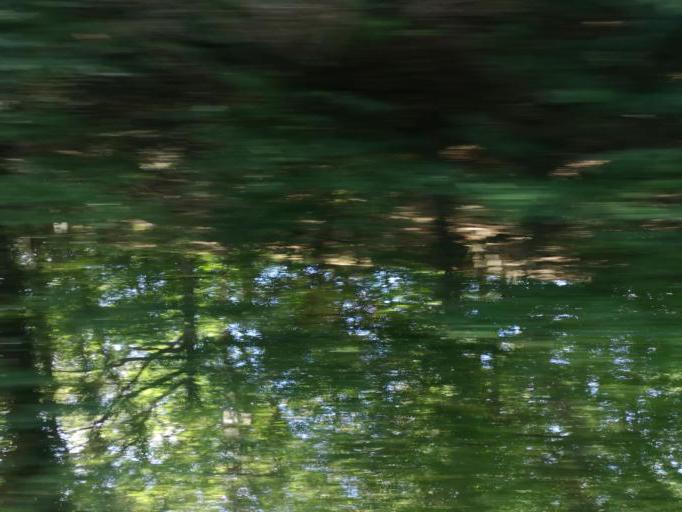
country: DE
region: North Rhine-Westphalia
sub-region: Regierungsbezirk Koln
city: Nideggen
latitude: 50.7083
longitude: 6.4408
